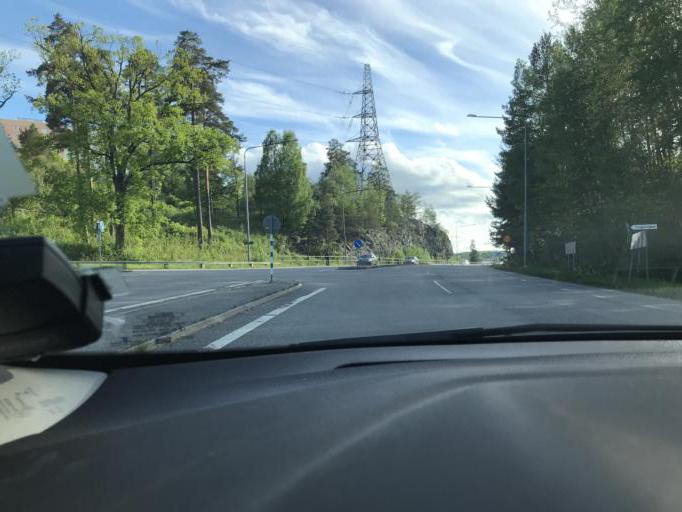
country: SE
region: Stockholm
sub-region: Botkyrka Kommun
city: Alby
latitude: 59.2443
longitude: 17.8414
